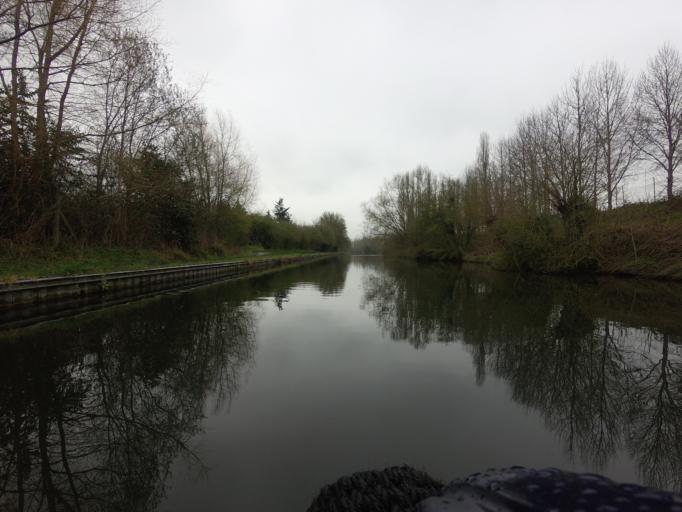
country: GB
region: England
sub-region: Hertfordshire
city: Kings Langley
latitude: 51.7223
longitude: -0.4498
